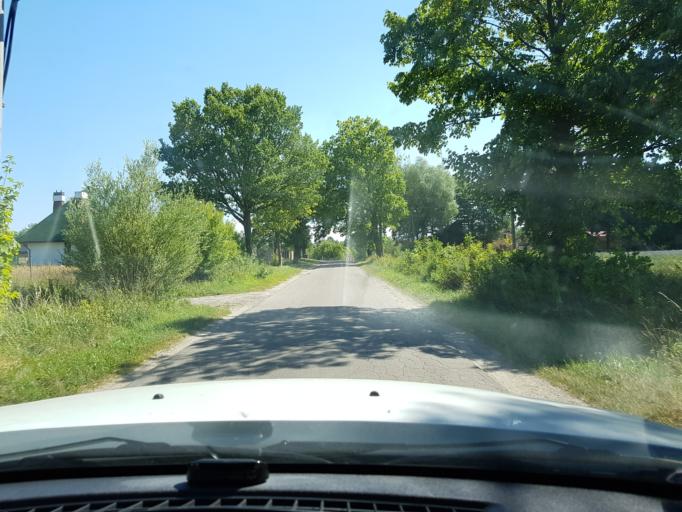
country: PL
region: West Pomeranian Voivodeship
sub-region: Powiat koszalinski
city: Mielno
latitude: 54.1750
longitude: 16.0789
